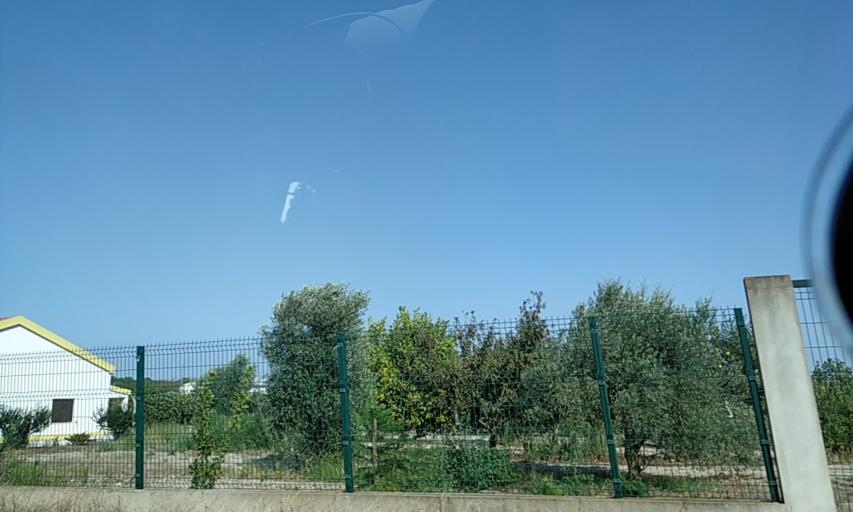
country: PT
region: Santarem
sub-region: Coruche
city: Coruche
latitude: 38.8232
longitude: -8.5665
